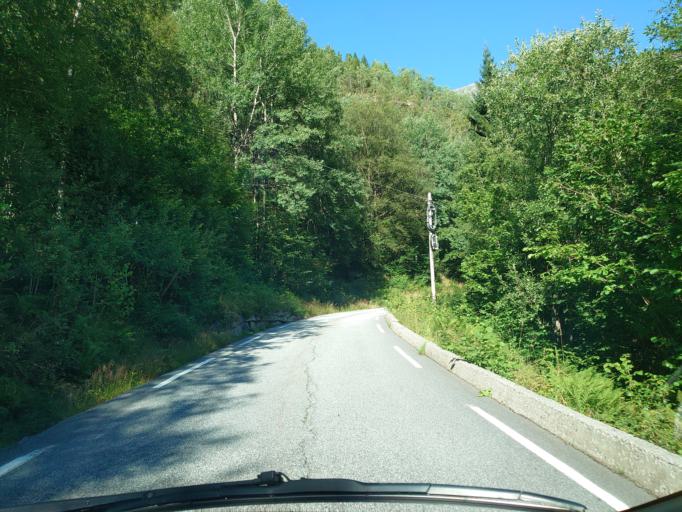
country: NO
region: Hordaland
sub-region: Vaksdal
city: Dale
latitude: 60.5870
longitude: 5.8451
